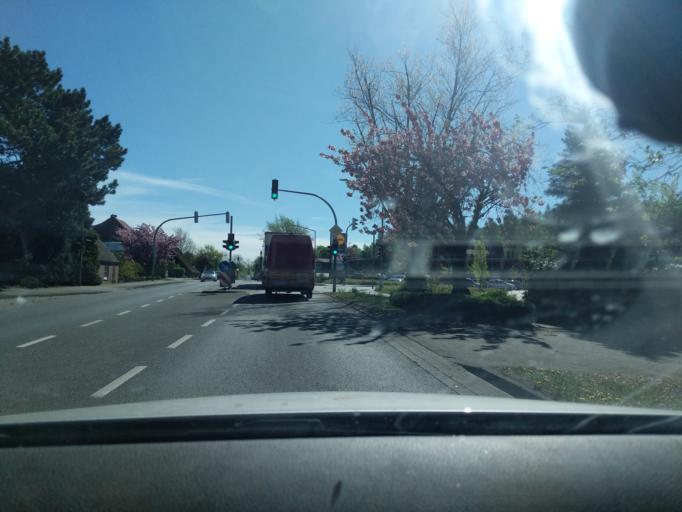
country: DE
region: Lower Saxony
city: Nottensdorf
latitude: 53.4838
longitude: 9.6219
